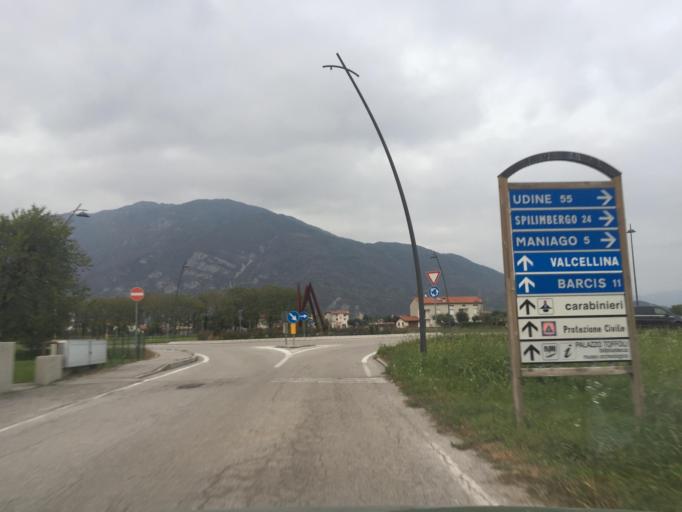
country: IT
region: Friuli Venezia Giulia
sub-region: Provincia di Pordenone
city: Montereale Valcellina
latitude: 46.1521
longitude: 12.6615
